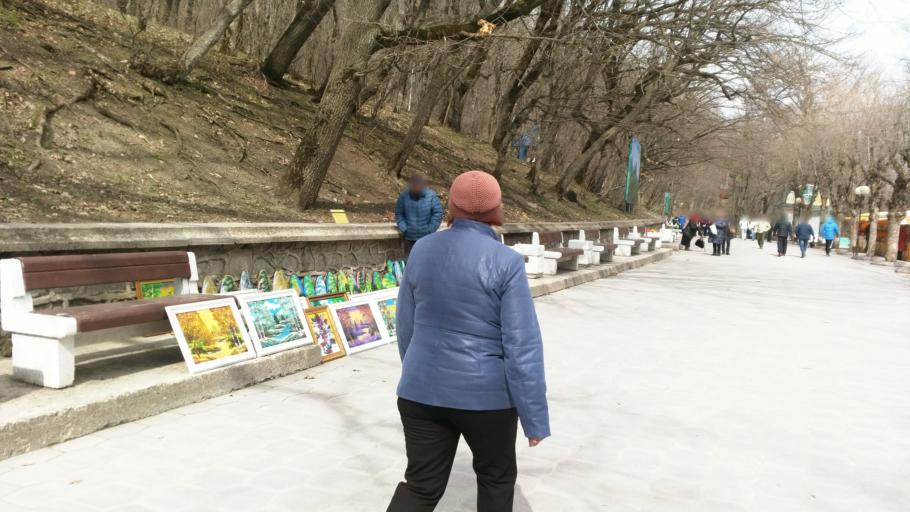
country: RU
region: Stavropol'skiy
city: Zheleznovodsk
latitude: 44.1358
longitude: 43.0330
